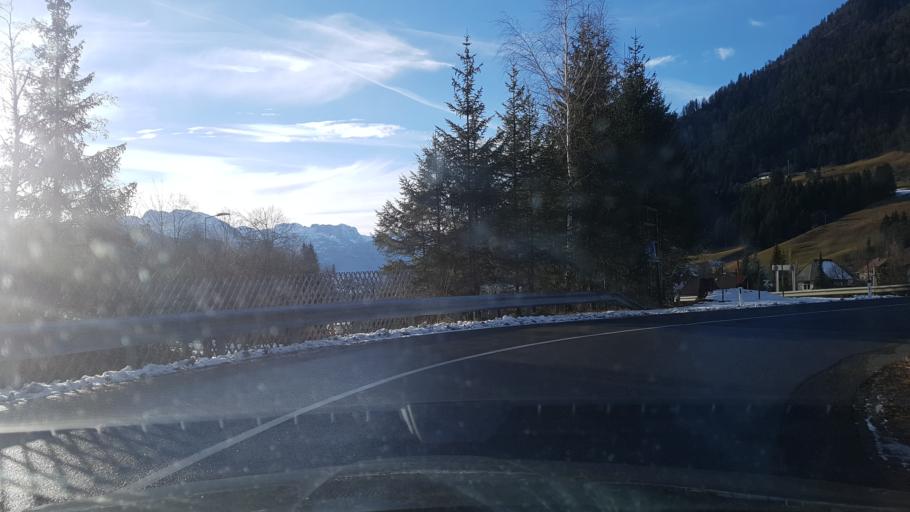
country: AT
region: Salzburg
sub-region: Politischer Bezirk Salzburg-Umgebung
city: Strobl
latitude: 47.5915
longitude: 13.4699
